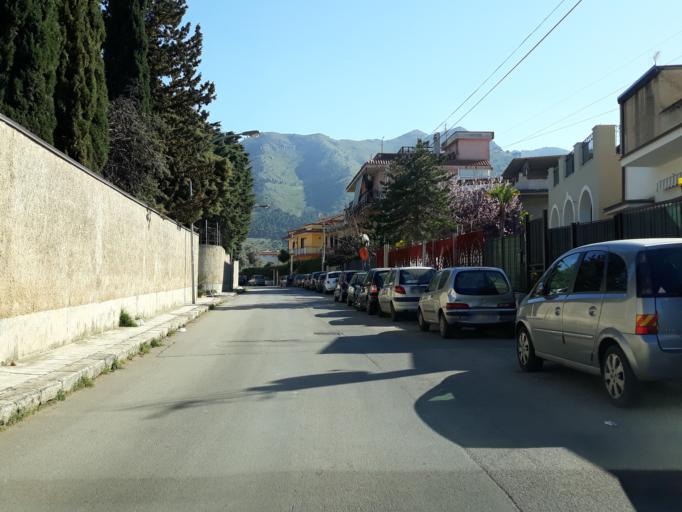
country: IT
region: Sicily
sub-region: Palermo
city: Villa Ciambra
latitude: 38.0859
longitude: 13.3447
